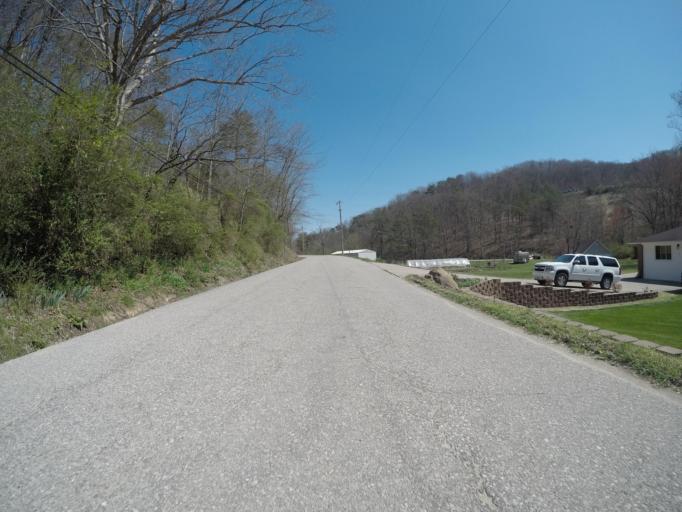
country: US
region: West Virginia
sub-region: Kanawha County
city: Charleston
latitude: 38.4132
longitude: -81.5711
